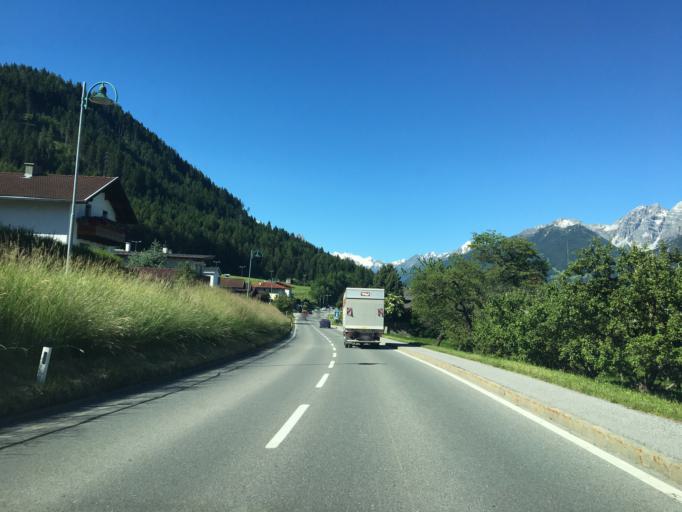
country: AT
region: Tyrol
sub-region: Politischer Bezirk Innsbruck Land
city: Schoenberg im Stubaital
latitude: 47.1854
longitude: 11.4022
